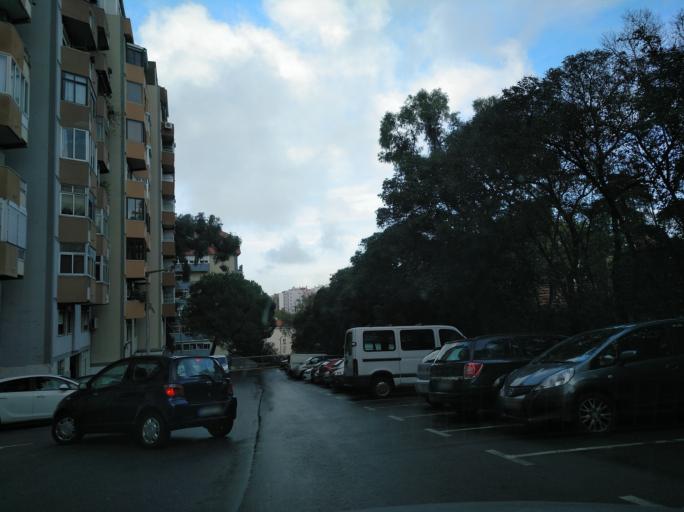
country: PT
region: Lisbon
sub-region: Odivelas
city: Pontinha
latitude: 38.7538
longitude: -9.1775
